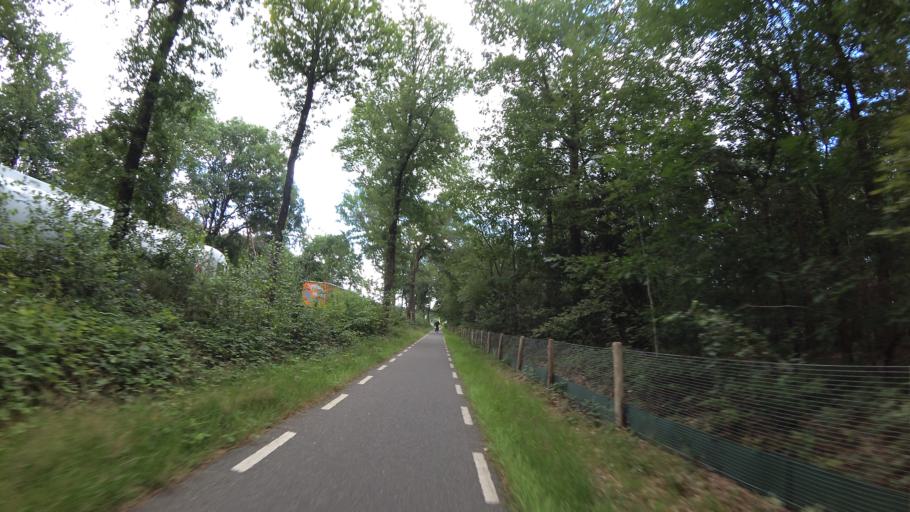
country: NL
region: North Brabant
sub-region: Gemeente Dongen
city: Dongen
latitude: 51.5895
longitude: 4.9019
